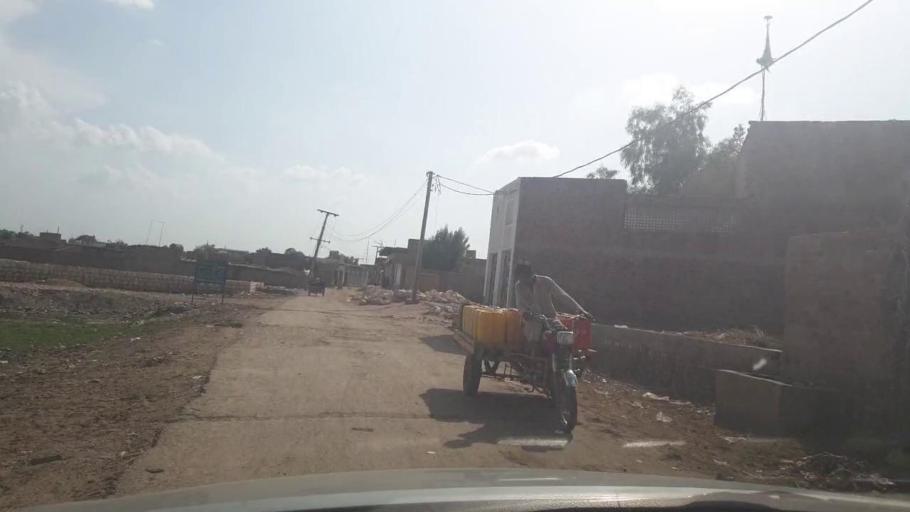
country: PK
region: Sindh
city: Khairpur
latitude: 27.5275
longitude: 68.7708
